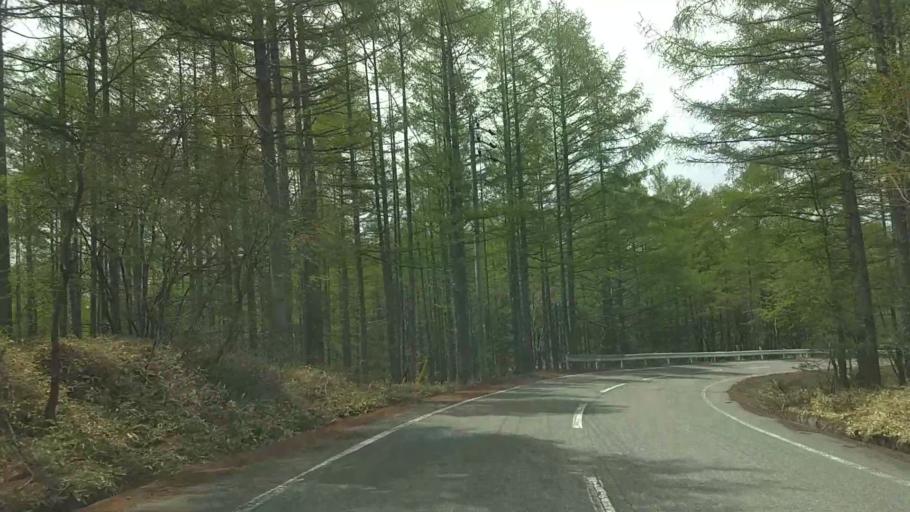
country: JP
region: Nagano
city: Chino
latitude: 36.0491
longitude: 138.3103
